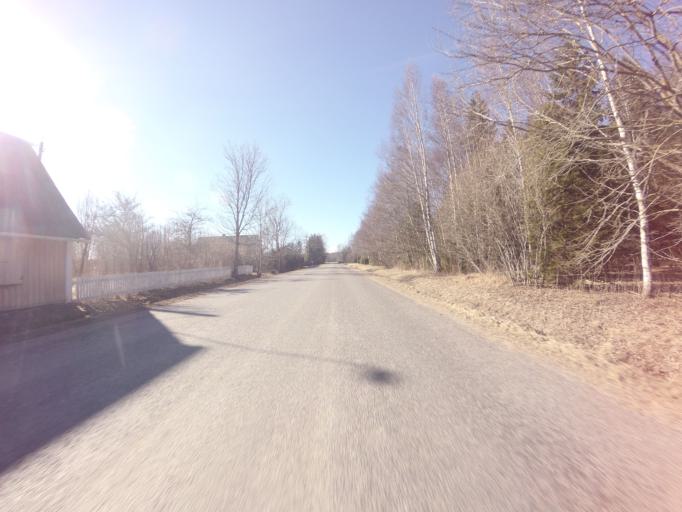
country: EE
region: Saare
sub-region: Kuressaare linn
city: Kuressaare
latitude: 58.5743
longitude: 22.6548
